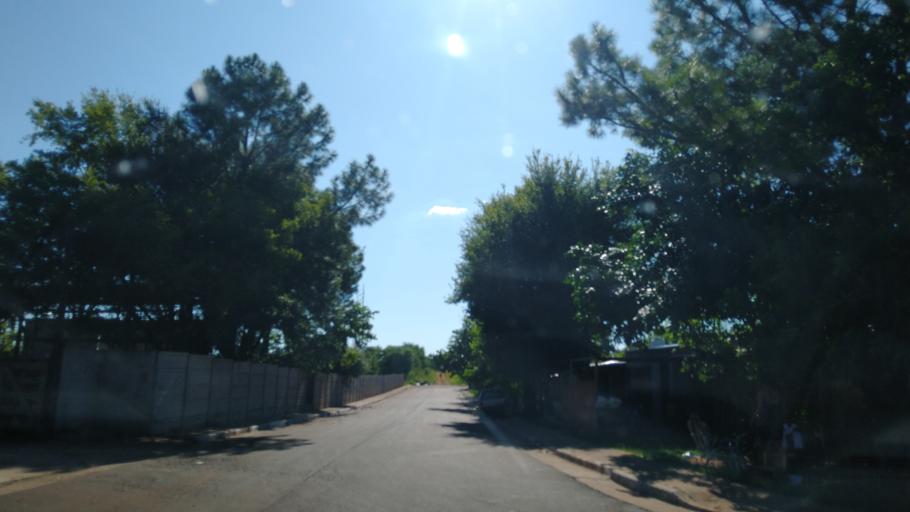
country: AR
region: Misiones
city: Garupa
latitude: -27.4906
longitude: -55.8211
